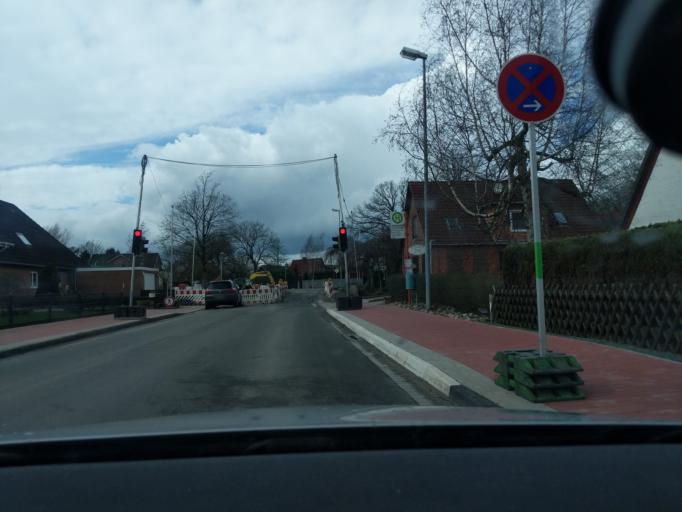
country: DE
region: Lower Saxony
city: Stade
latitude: 53.6172
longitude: 9.4622
